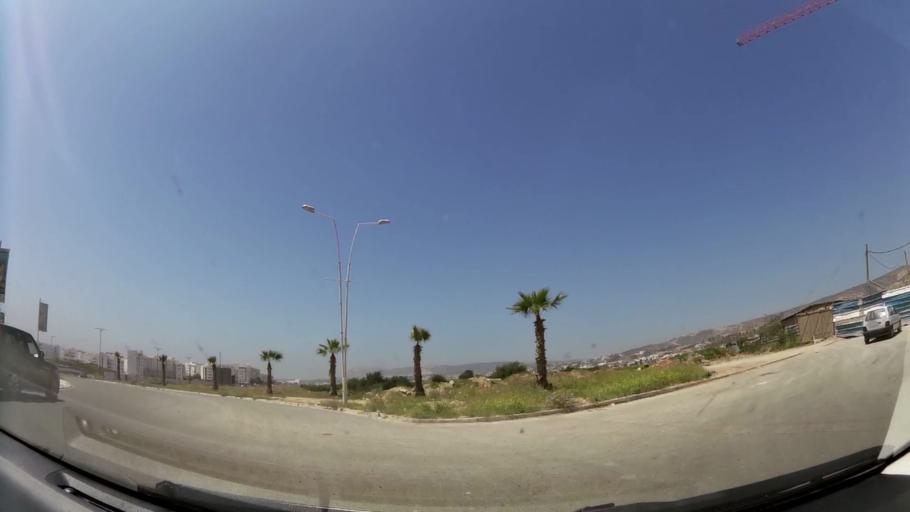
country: MA
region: Oued ed Dahab-Lagouira
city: Dakhla
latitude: 30.4389
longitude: -9.5658
